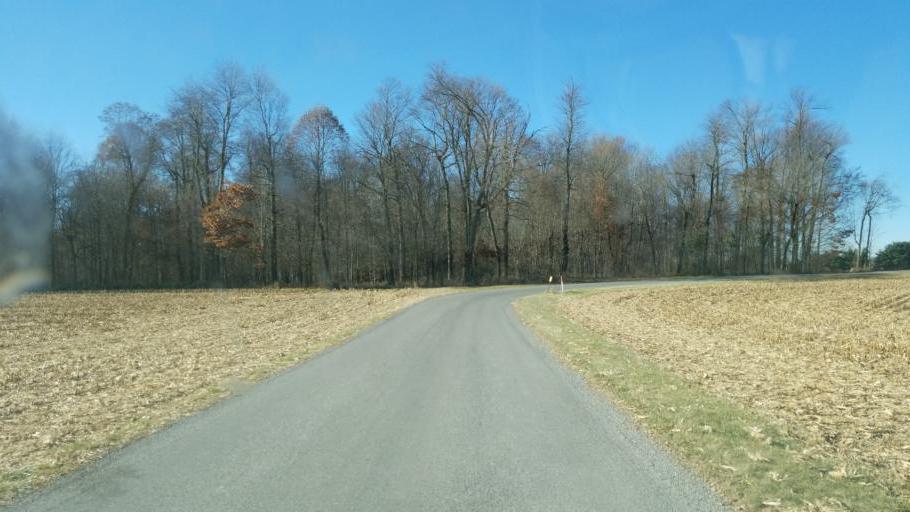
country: US
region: Ohio
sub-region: Richland County
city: Shelby
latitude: 40.9380
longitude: -82.6134
